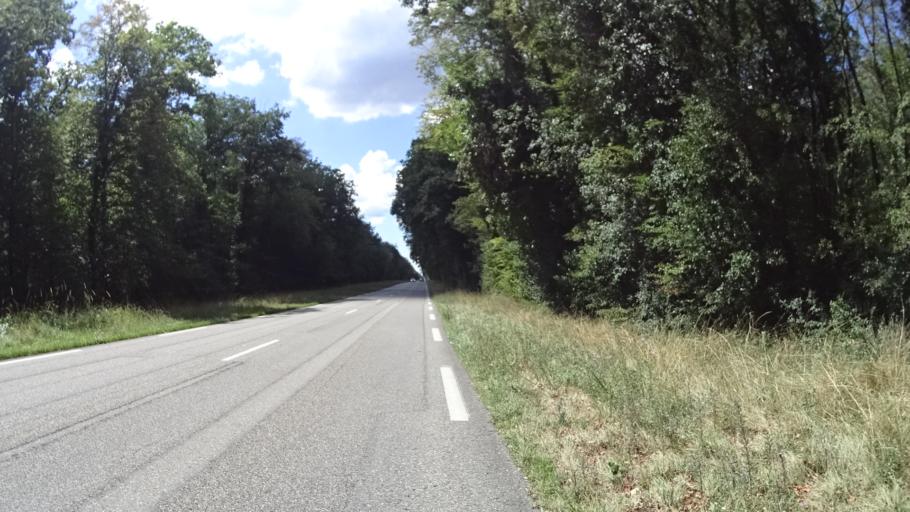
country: FR
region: Alsace
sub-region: Departement du Haut-Rhin
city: Ottmarsheim
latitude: 47.7781
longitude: 7.4849
